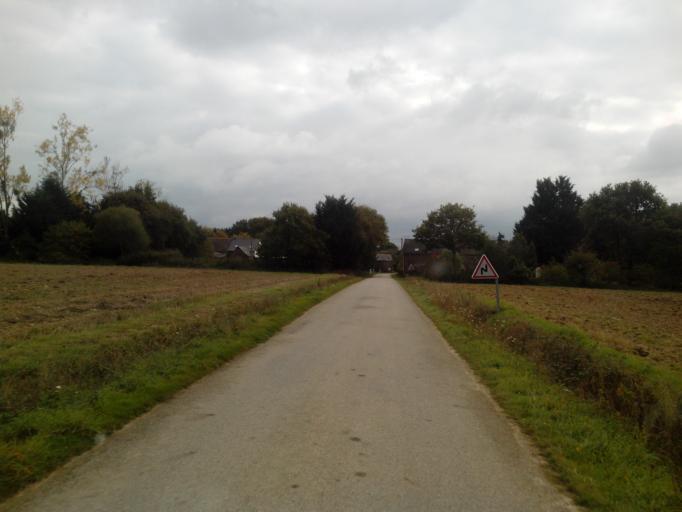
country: FR
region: Brittany
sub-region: Departement du Morbihan
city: Guilliers
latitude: 48.0772
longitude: -2.3505
